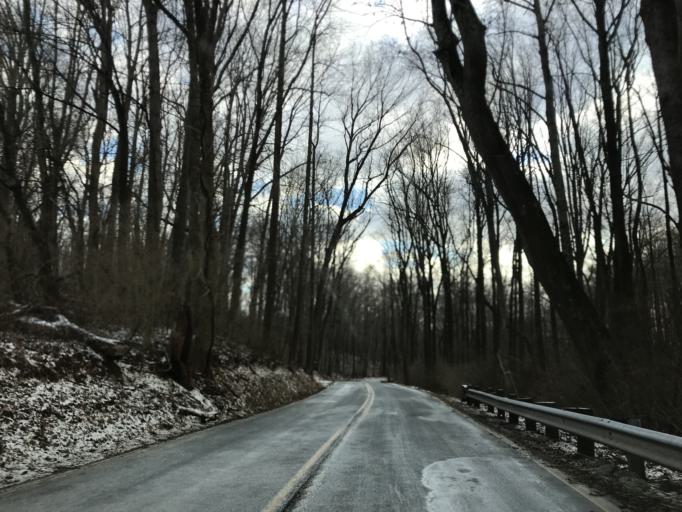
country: US
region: Maryland
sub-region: Harford County
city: Bel Air North
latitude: 39.6339
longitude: -76.3760
